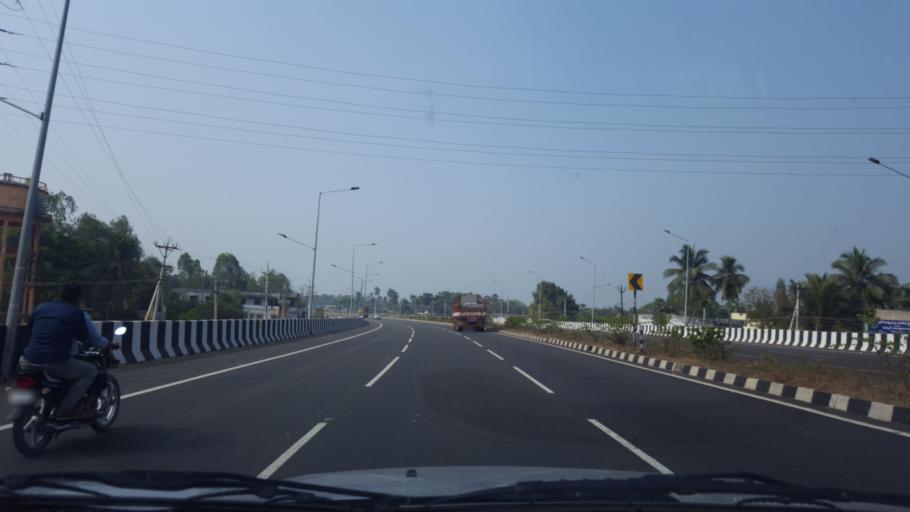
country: IN
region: Andhra Pradesh
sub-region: Vizianagaram District
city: Vizianagaram
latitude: 18.0283
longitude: 83.4931
